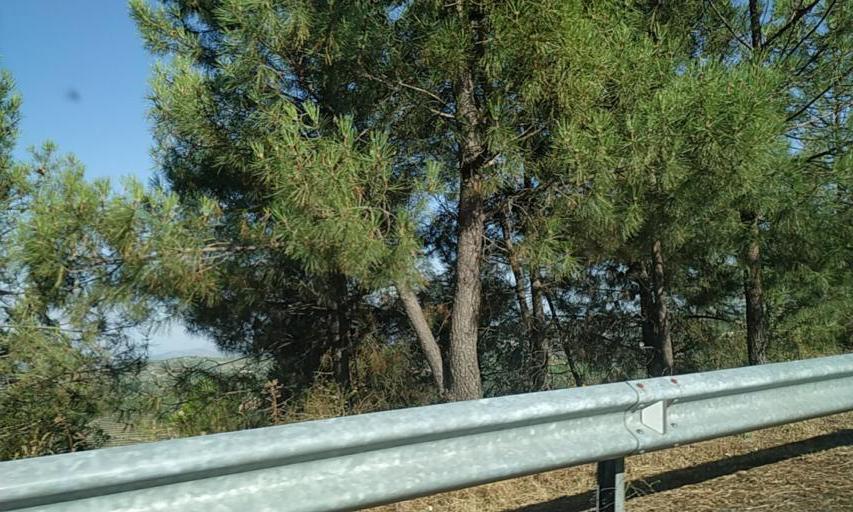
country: PT
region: Viseu
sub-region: Sao Joao da Pesqueira
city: Sao Joao da Pesqueira
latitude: 41.1634
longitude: -7.4322
